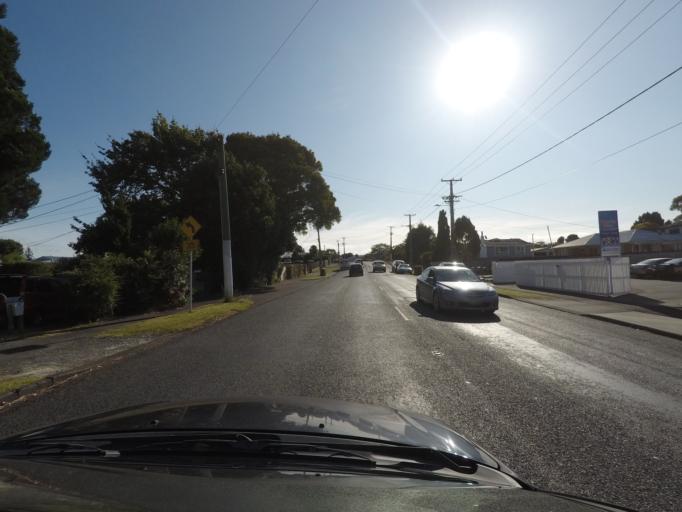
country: NZ
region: Auckland
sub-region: Auckland
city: Rosebank
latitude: -36.8626
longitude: 174.6120
